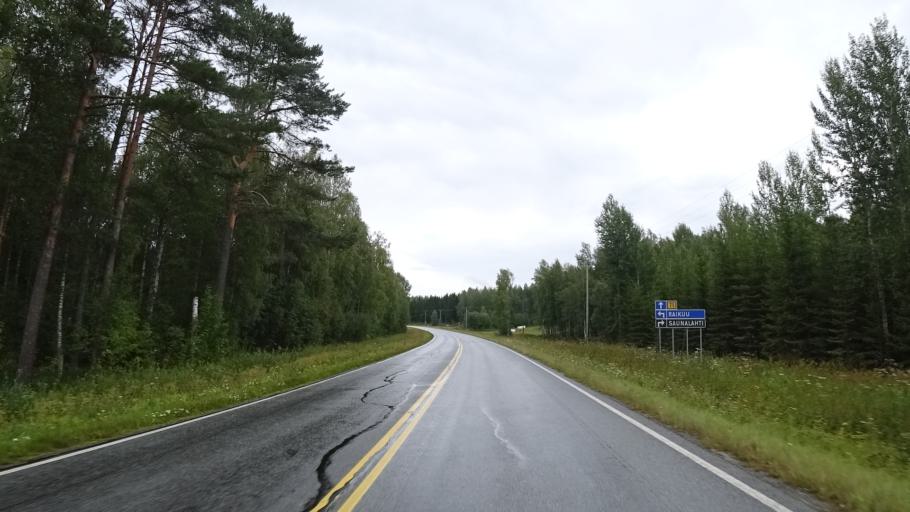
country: FI
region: Southern Savonia
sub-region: Savonlinna
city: Kerimaeki
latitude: 62.0368
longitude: 29.5368
